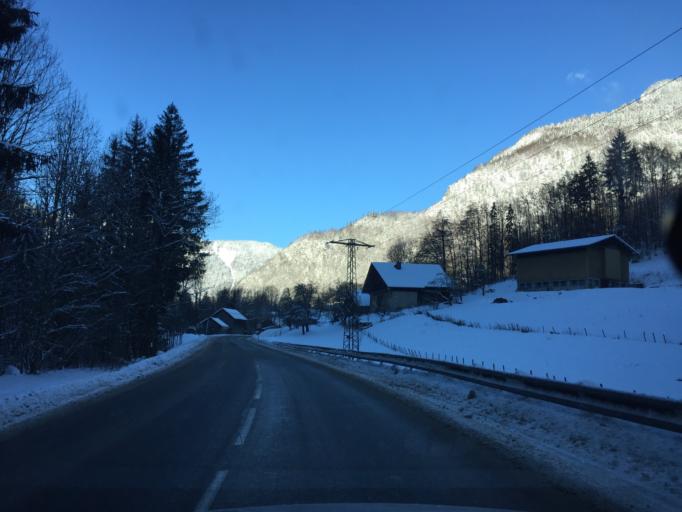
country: FR
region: Rhone-Alpes
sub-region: Departement de la Haute-Savoie
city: Abondance
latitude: 46.2822
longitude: 6.7058
